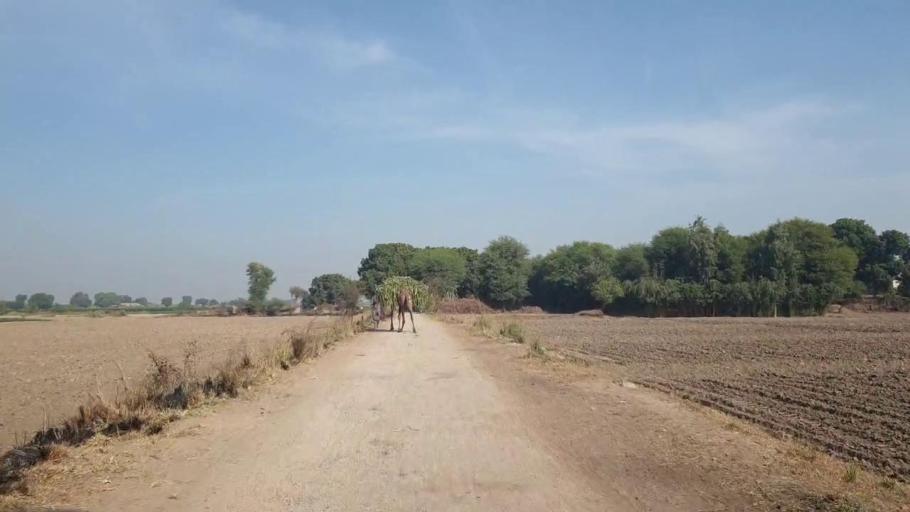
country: PK
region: Sindh
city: Matiari
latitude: 25.6778
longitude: 68.3480
